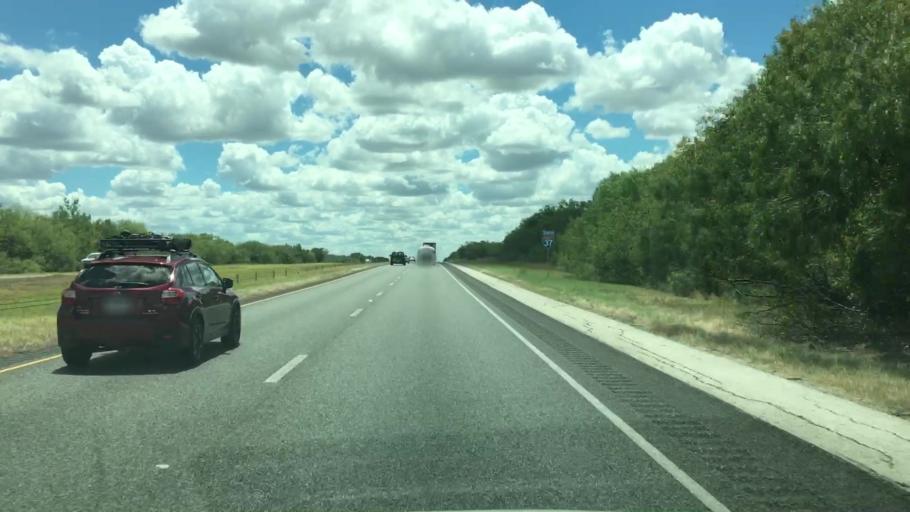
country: US
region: Texas
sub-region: Bexar County
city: Elmendorf
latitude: 29.1350
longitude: -98.4298
